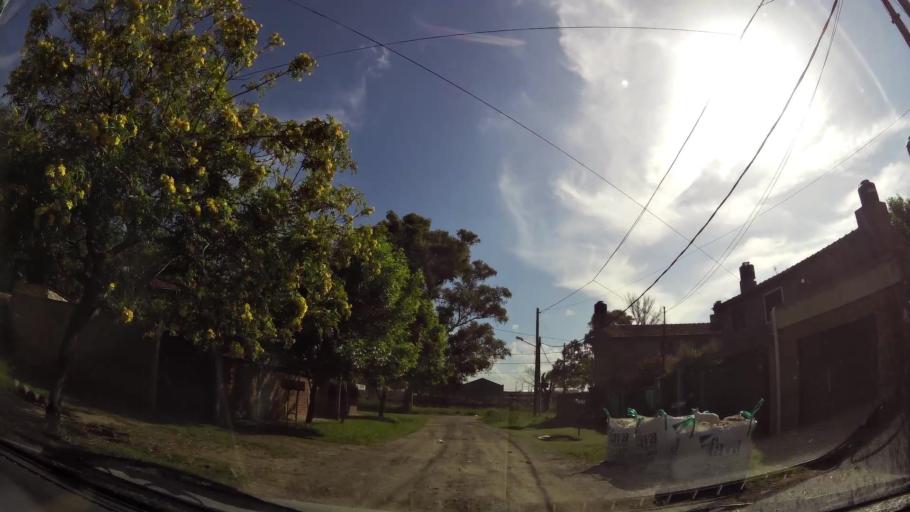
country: AR
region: Buenos Aires
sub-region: Partido de Quilmes
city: Quilmes
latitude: -34.7953
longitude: -58.2444
